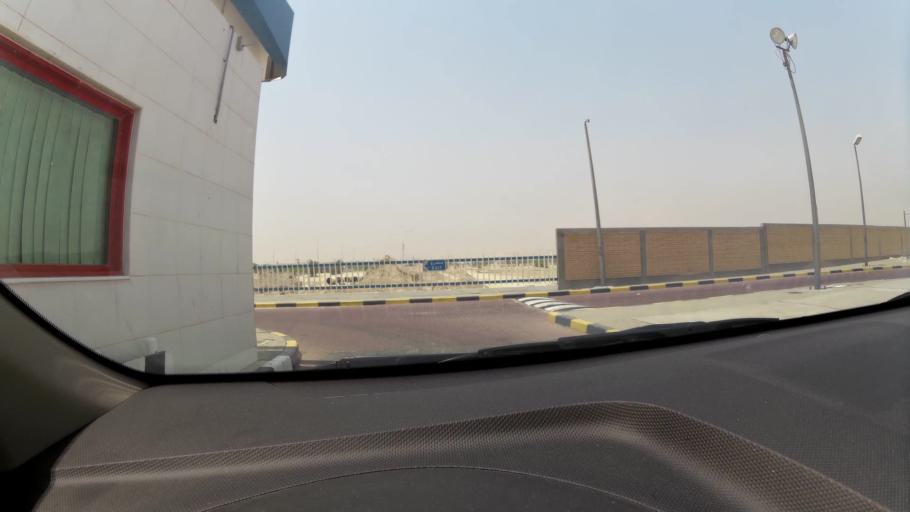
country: KW
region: Muhafazat al Jahra'
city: Al Jahra'
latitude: 29.3646
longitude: 47.6714
